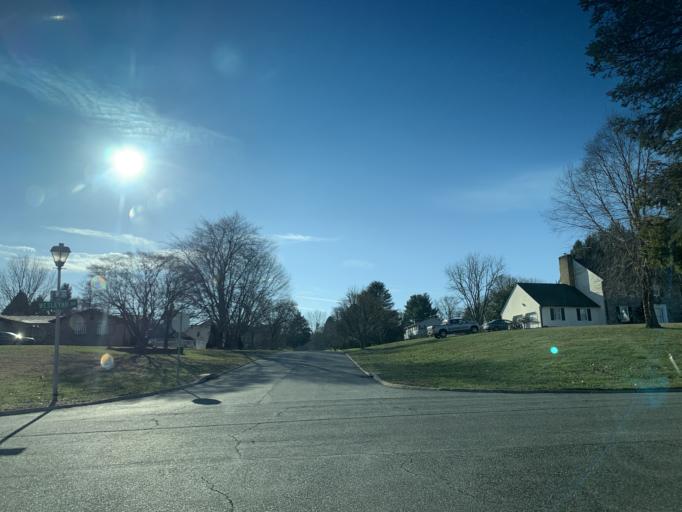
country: US
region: Maryland
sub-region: Harford County
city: South Bel Air
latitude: 39.5686
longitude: -76.2641
